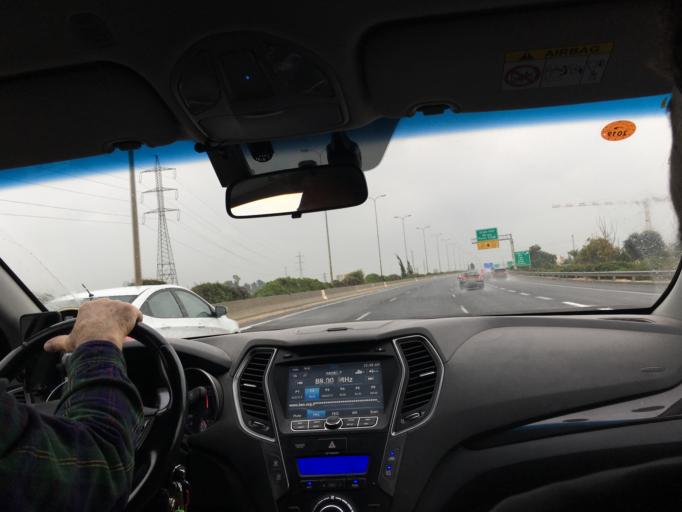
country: IL
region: Tel Aviv
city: Ramat HaSharon
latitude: 32.1205
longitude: 34.8673
